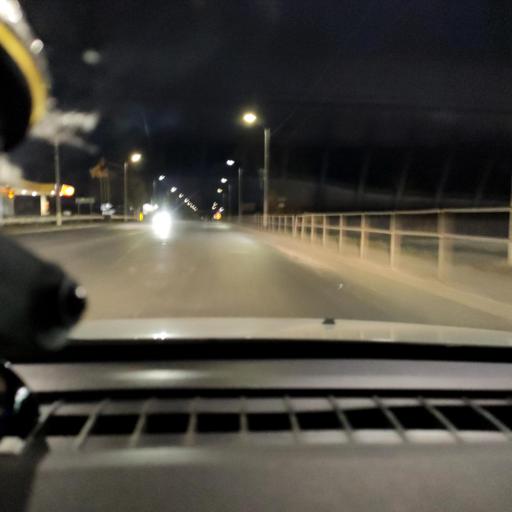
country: RU
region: Samara
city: Novokuybyshevsk
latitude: 53.0903
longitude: 49.9418
